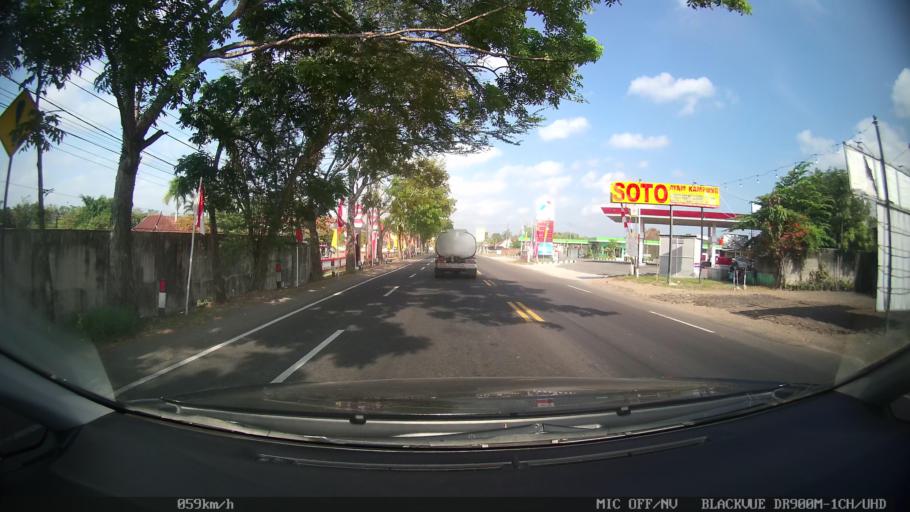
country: ID
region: Daerah Istimewa Yogyakarta
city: Godean
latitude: -7.8259
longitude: 110.2267
